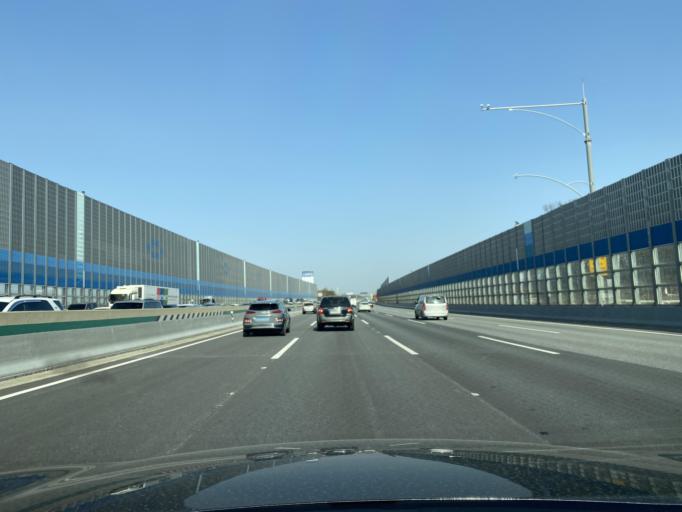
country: KR
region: Gyeonggi-do
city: Hwaseong-si
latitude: 37.0210
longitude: 126.8725
